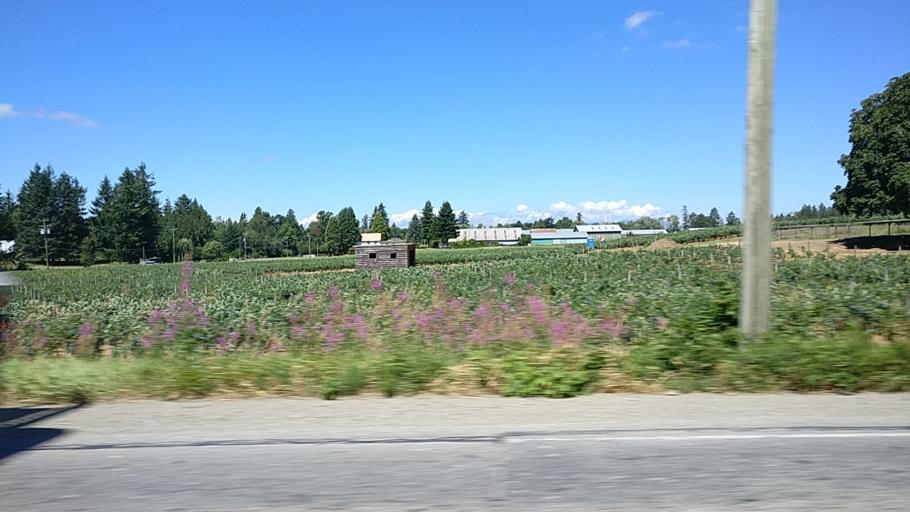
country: CA
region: British Columbia
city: Aldergrove
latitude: 49.0314
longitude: -122.4692
